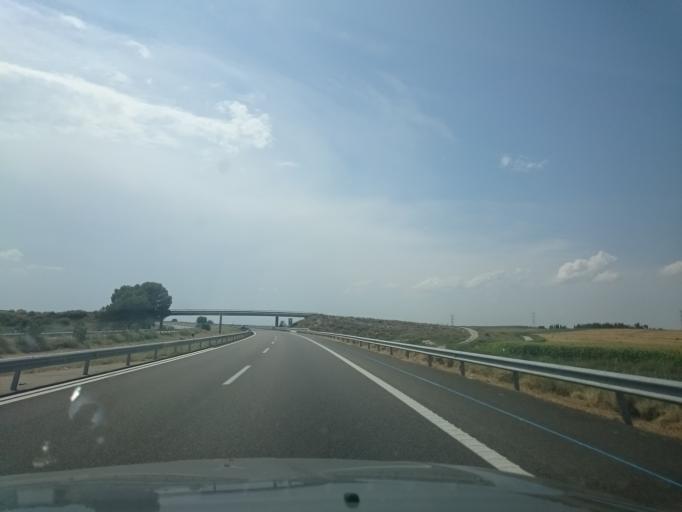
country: ES
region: Aragon
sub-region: Provincia de Huesca
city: Penalba
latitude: 41.5179
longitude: -0.0842
